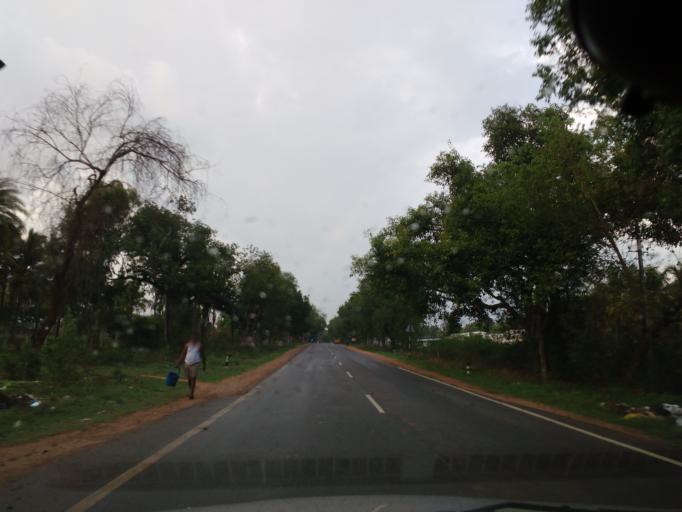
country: IN
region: Karnataka
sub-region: Tumkur
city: Tiptur
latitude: 13.2765
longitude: 76.5224
